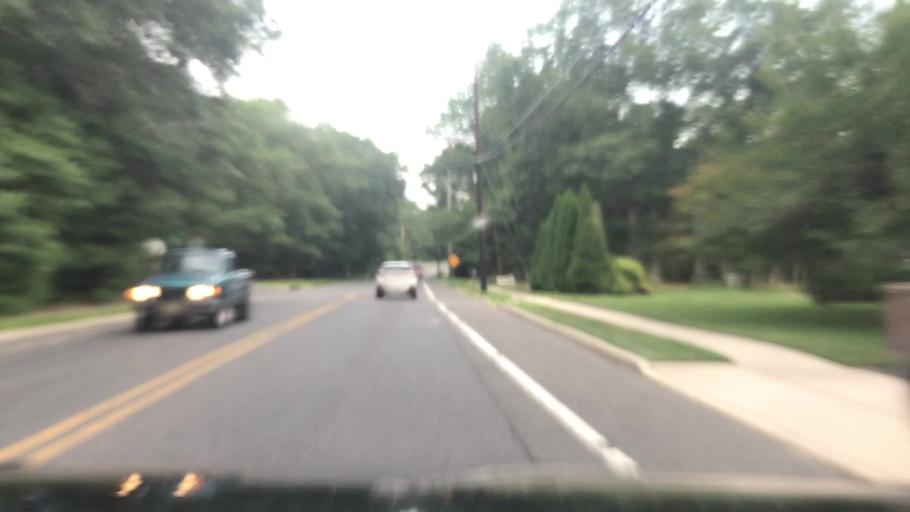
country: US
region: New Jersey
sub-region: Ocean County
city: Lakewood
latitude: 40.1051
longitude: -74.2737
